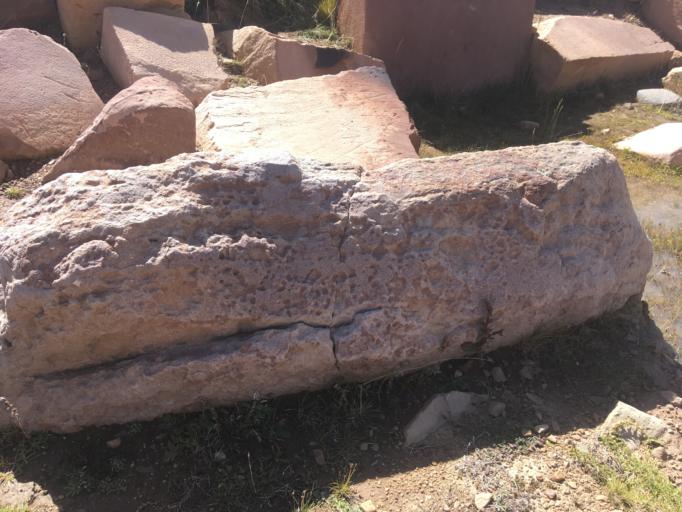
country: BO
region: La Paz
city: San Pedro
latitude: -16.2633
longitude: -68.8732
